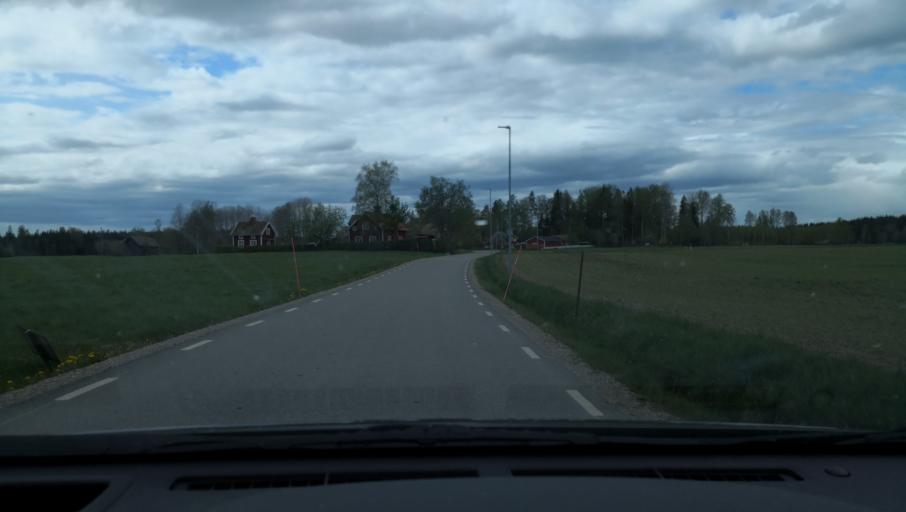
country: SE
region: Dalarna
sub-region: Avesta Kommun
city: Avesta
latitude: 60.0230
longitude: 16.2668
